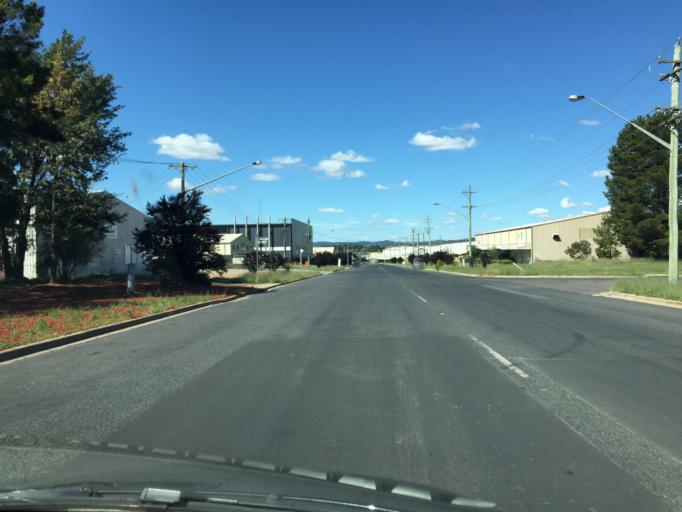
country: AU
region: Australian Capital Territory
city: Macarthur
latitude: -35.3908
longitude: 149.1674
